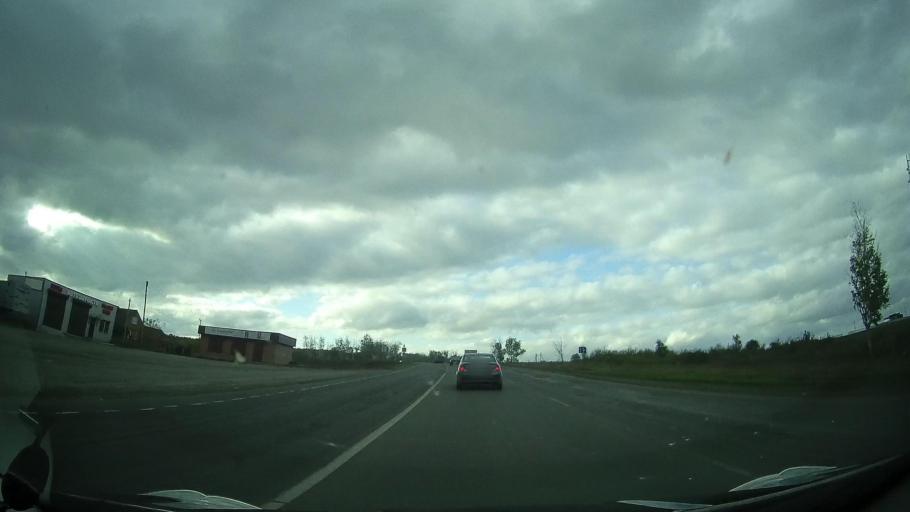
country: RU
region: Rostov
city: Kagal'nitskaya
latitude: 46.8872
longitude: 40.1415
